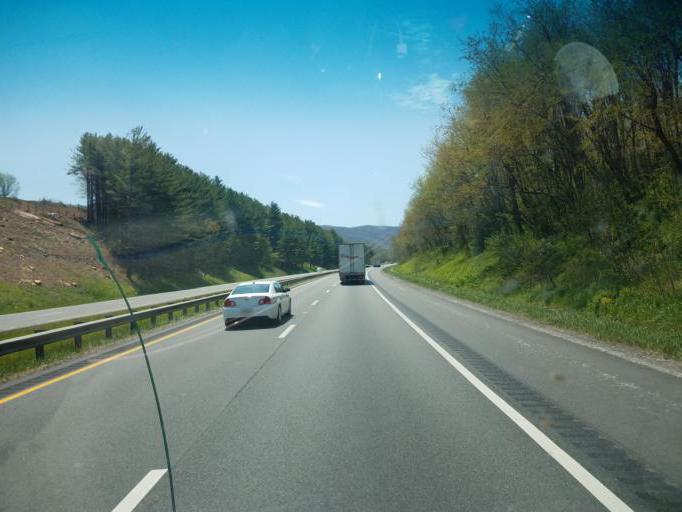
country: US
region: Virginia
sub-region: Bland County
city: Bland
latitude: 37.0656
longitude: -81.1276
